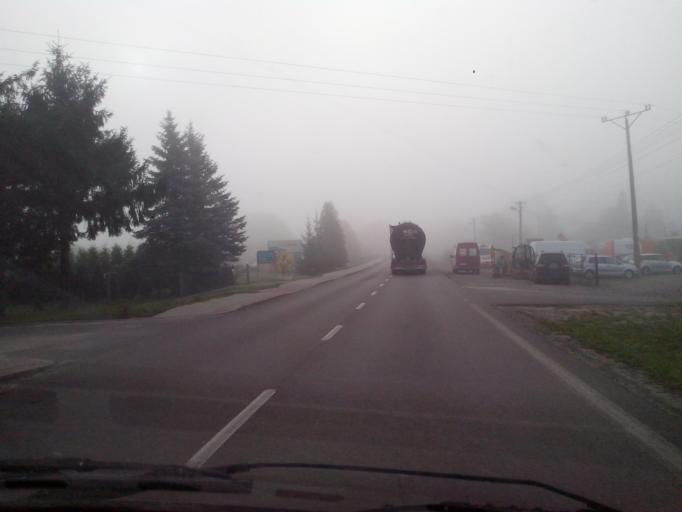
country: PL
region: Subcarpathian Voivodeship
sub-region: Przemysl
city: Przemysl
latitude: 49.7929
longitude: 22.7220
